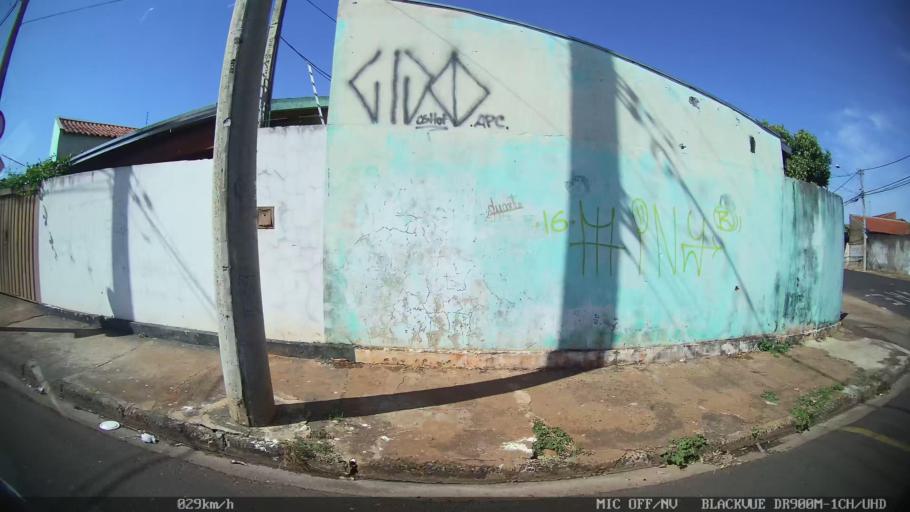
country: BR
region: Sao Paulo
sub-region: Sao Jose Do Rio Preto
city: Sao Jose do Rio Preto
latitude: -20.7766
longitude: -49.4188
